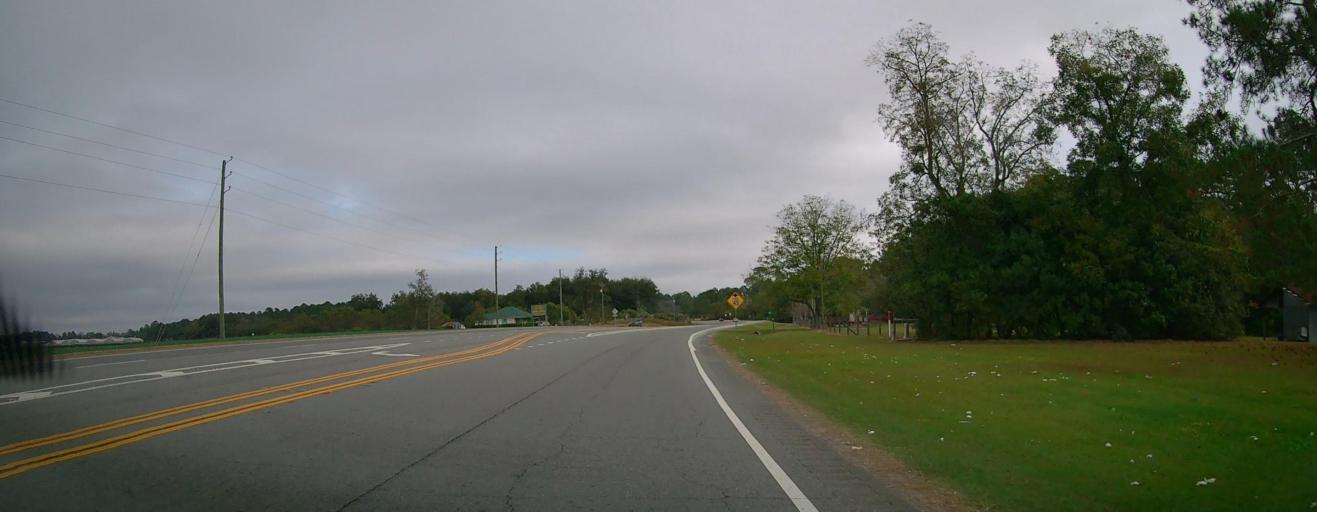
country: US
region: Georgia
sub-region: Tift County
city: Omega
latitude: 31.3333
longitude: -83.6089
